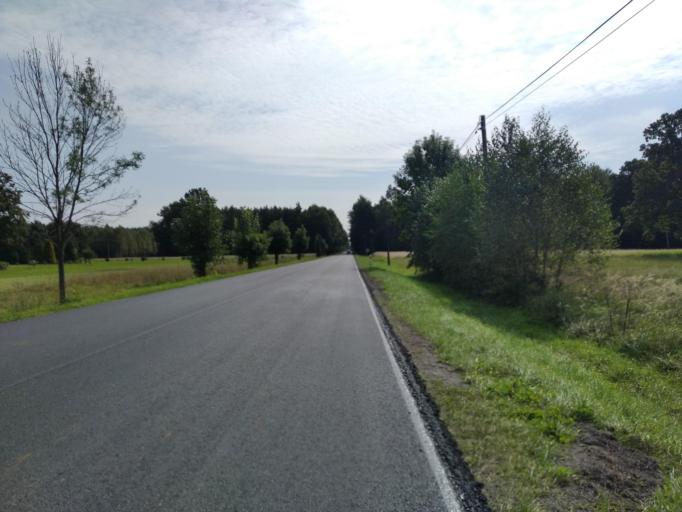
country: PL
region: Subcarpathian Voivodeship
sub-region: Powiat ropczycko-sedziszowski
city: Ostrow
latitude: 50.1542
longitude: 21.5611
